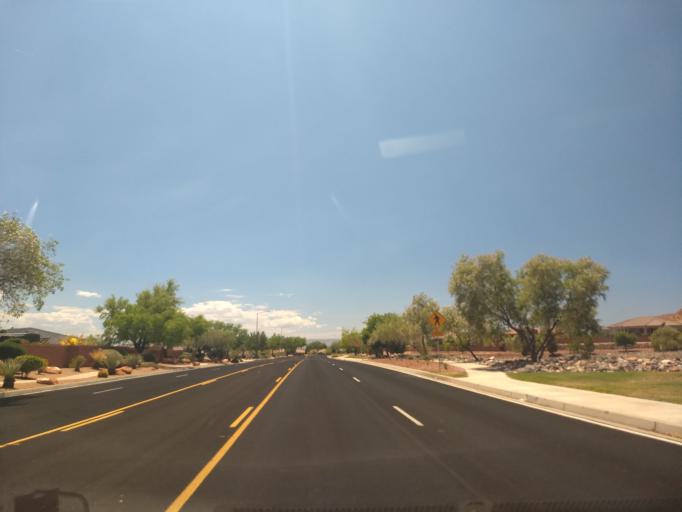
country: US
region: Utah
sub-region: Washington County
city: Washington
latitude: 37.1546
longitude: -113.5259
